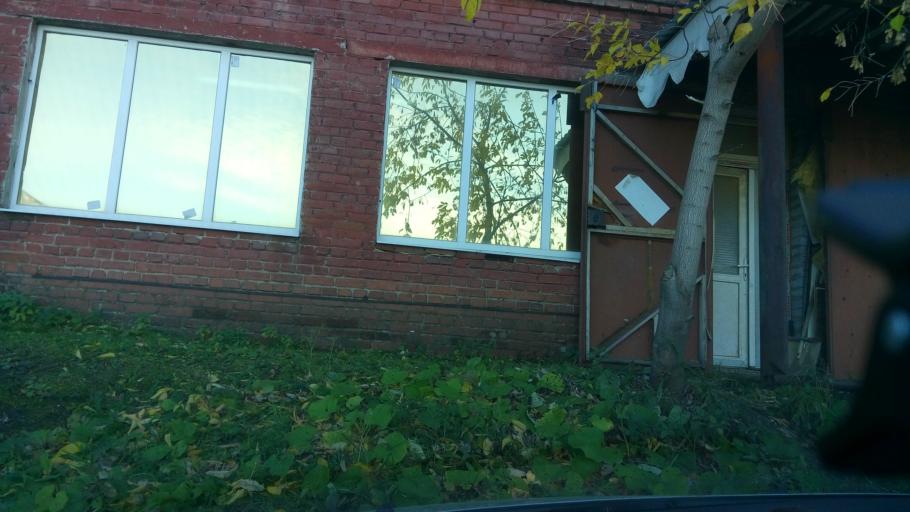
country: RU
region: Sverdlovsk
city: Sovkhoznyy
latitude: 56.7695
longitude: 60.6312
